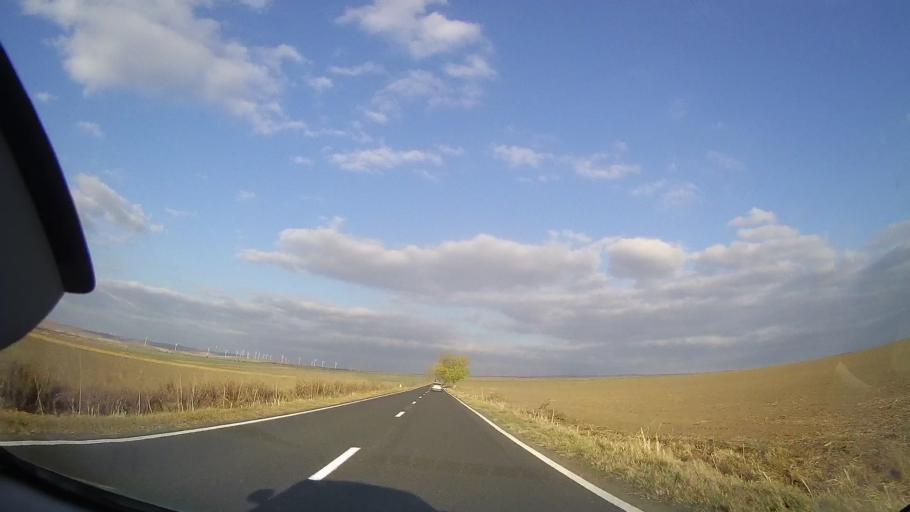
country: RO
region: Tulcea
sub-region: Comuna Topolog
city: Topolog
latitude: 44.8372
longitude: 28.2972
